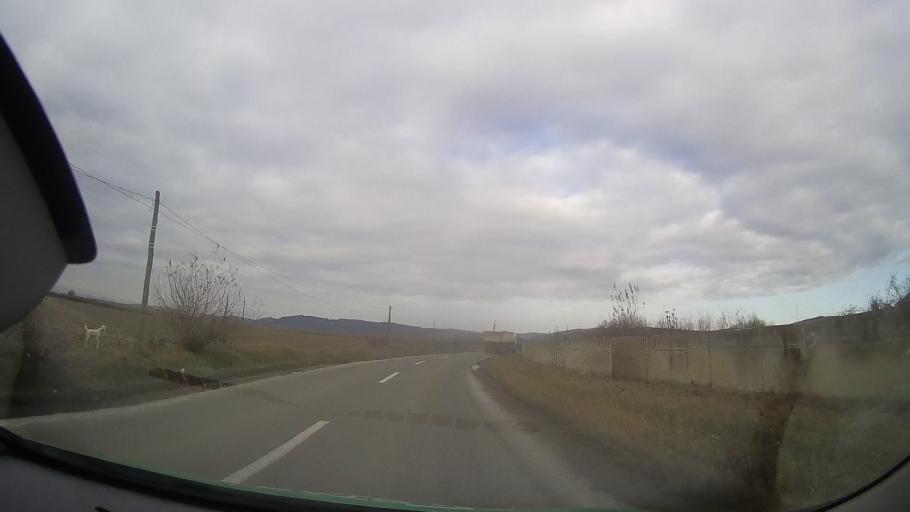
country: RO
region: Mures
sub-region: Comuna Iernut
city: Iernut
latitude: 46.4611
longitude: 24.2186
